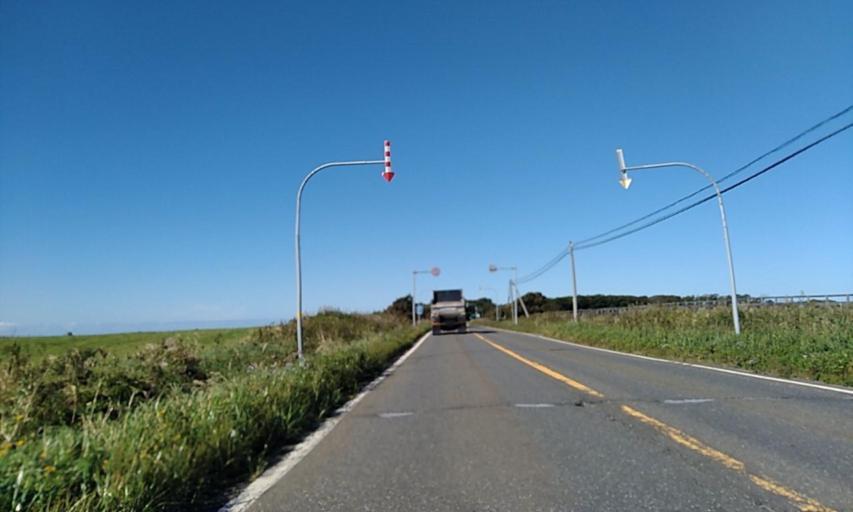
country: JP
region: Hokkaido
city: Shizunai-furukawacho
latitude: 42.4717
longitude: 142.1018
